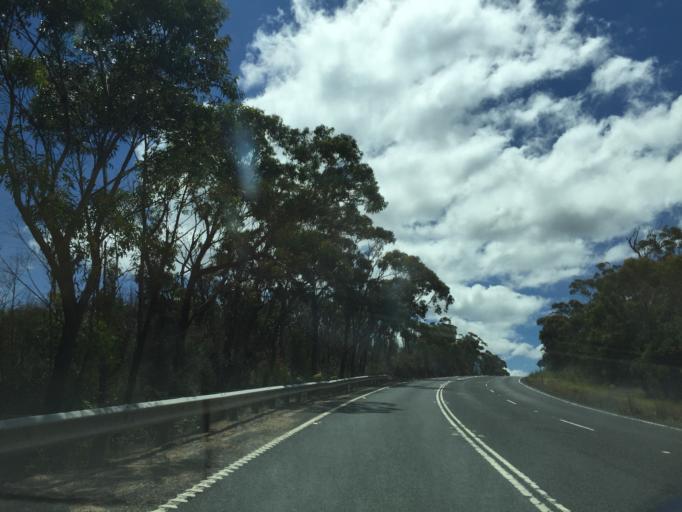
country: AU
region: New South Wales
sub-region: Blue Mountains Municipality
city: Blackheath
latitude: -33.5656
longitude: 150.3450
